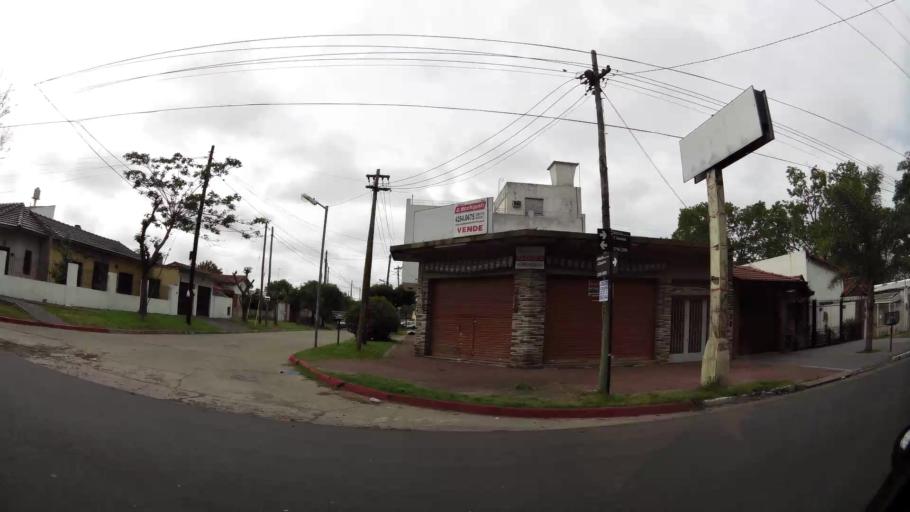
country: AR
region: Buenos Aires
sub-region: Partido de Quilmes
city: Quilmes
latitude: -34.7417
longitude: -58.2787
